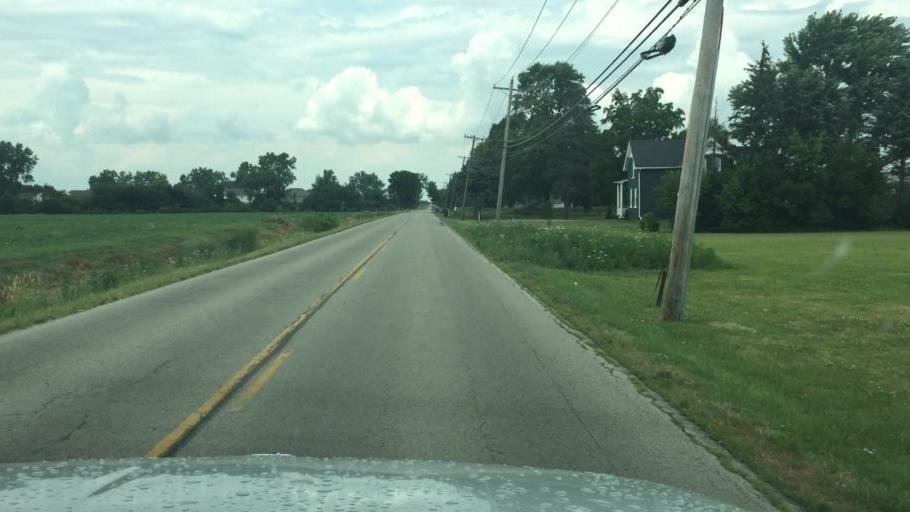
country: US
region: Ohio
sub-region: Wood County
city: Walbridge
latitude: 41.5790
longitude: -83.5277
